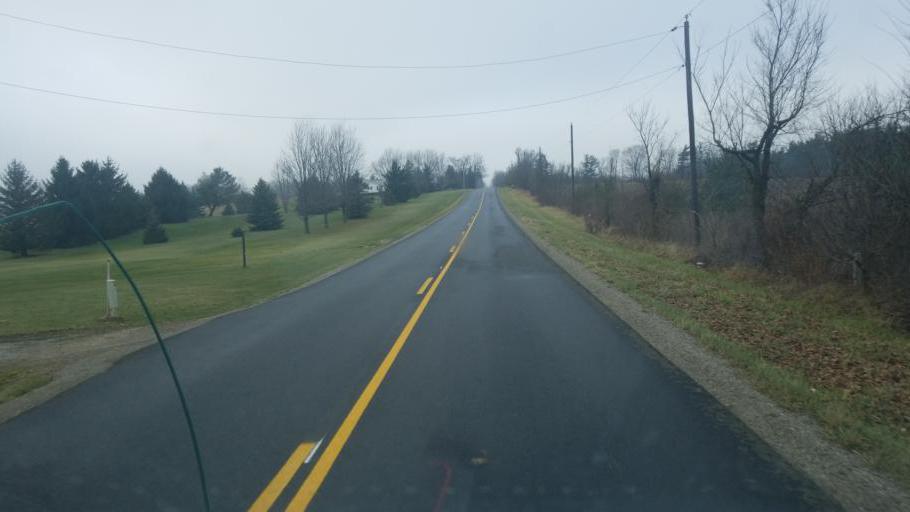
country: US
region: Ohio
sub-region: Champaign County
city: North Lewisburg
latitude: 40.2834
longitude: -83.5726
